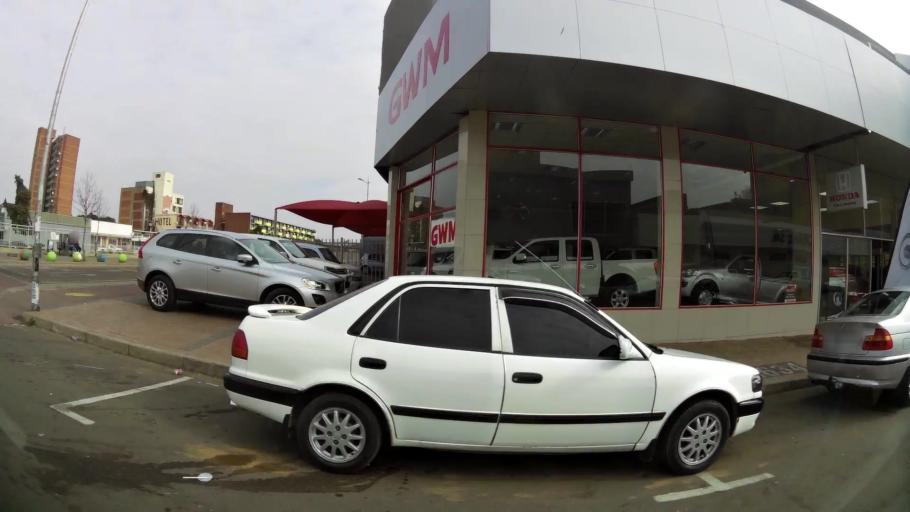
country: ZA
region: Orange Free State
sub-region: Mangaung Metropolitan Municipality
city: Bloemfontein
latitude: -29.1196
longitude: 26.2212
